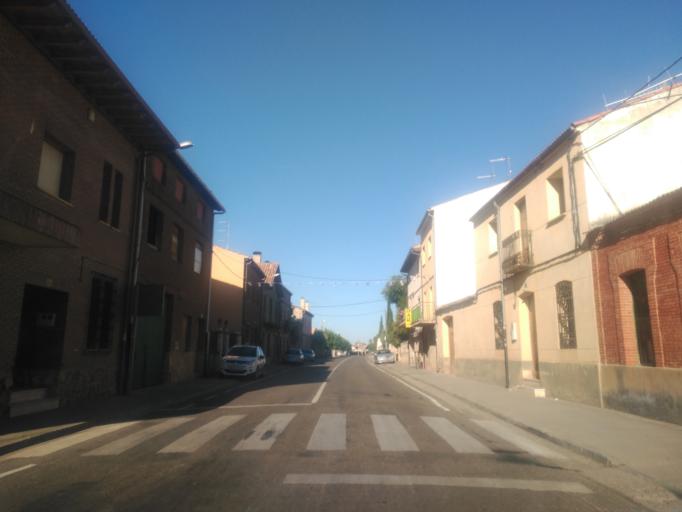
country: ES
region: Castille and Leon
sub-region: Provincia de Burgos
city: Zazuar
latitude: 41.6948
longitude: -3.5562
